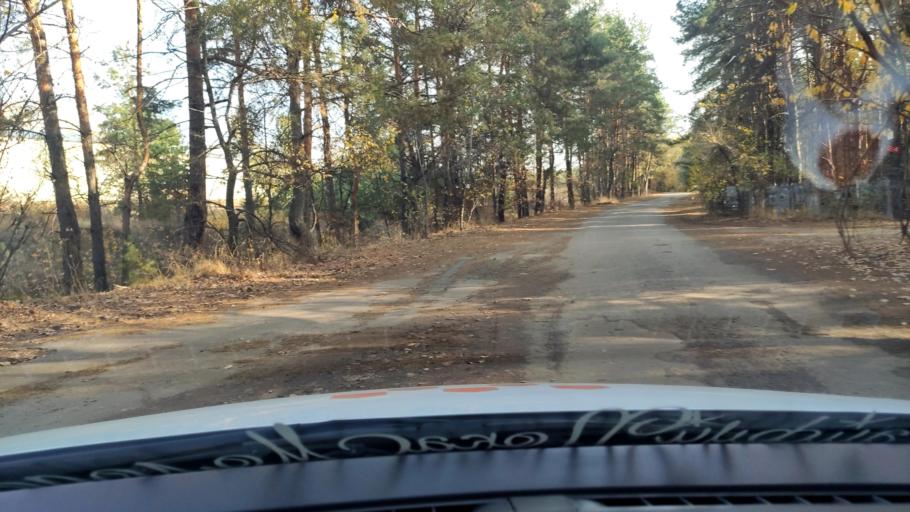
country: RU
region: Voronezj
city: Pridonskoy
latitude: 51.6695
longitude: 39.0964
